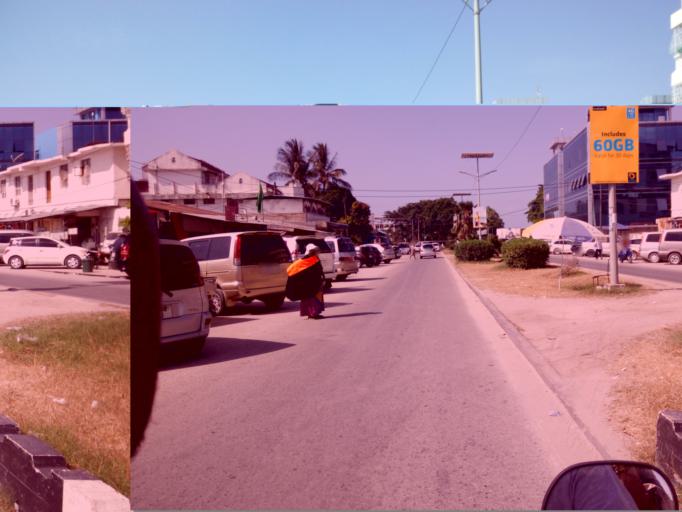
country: TZ
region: Zanzibar Urban/West
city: Zanzibar
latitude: -6.1601
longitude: 39.1989
